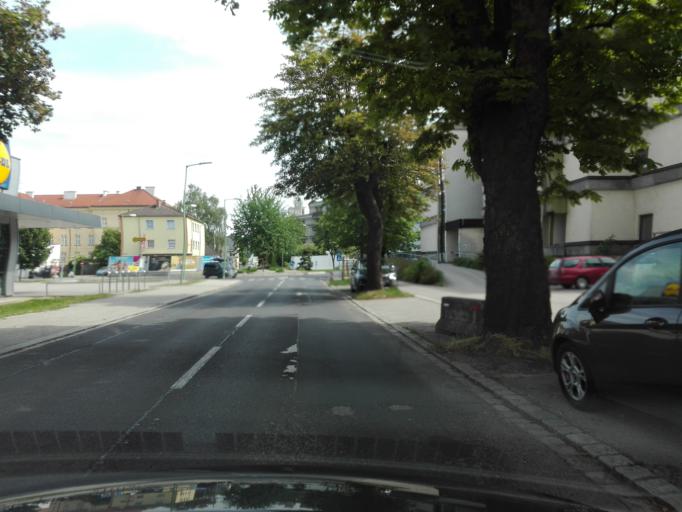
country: AT
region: Upper Austria
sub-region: Wels Stadt
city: Wels
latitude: 48.1646
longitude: 14.0329
